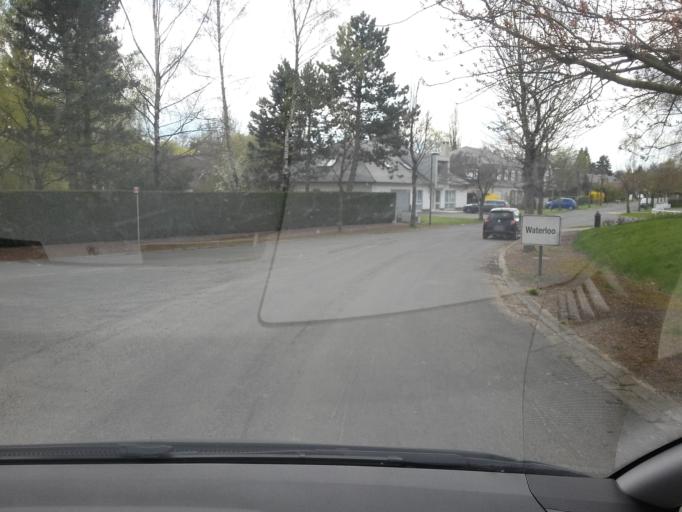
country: BE
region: Wallonia
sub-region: Province du Brabant Wallon
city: Waterloo
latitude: 50.7079
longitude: 4.4213
